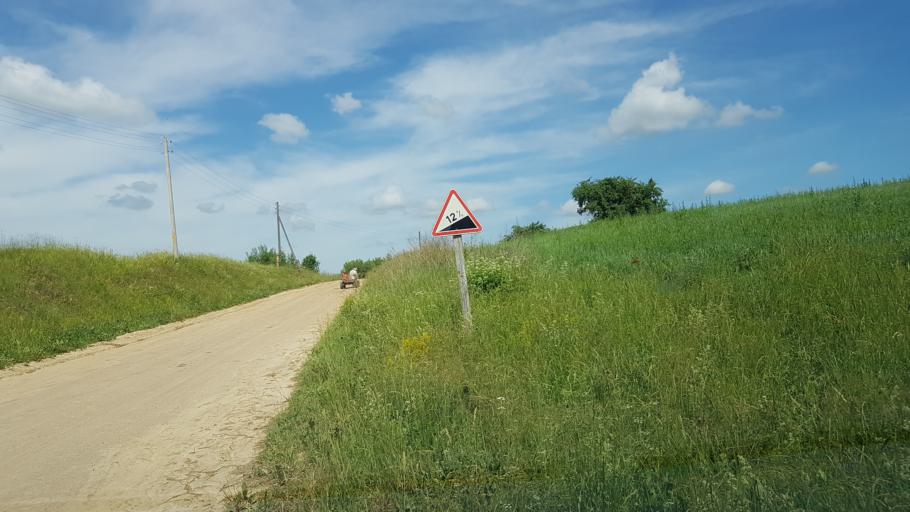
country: BY
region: Vitebsk
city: Dubrowna
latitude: 54.4861
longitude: 30.7976
